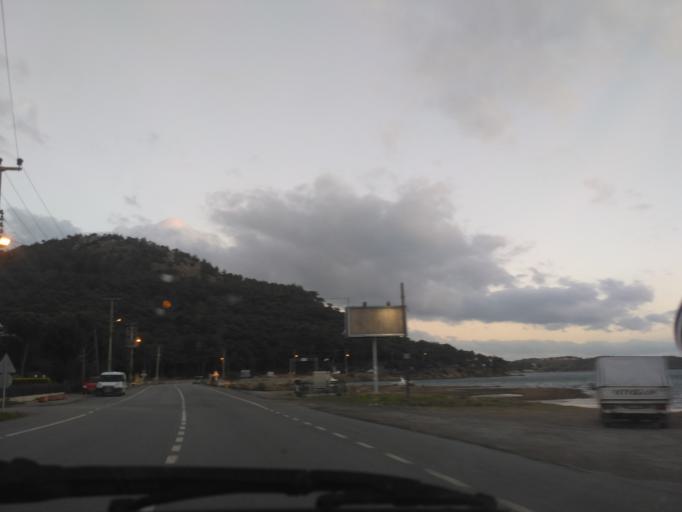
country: TR
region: Balikesir
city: Ayvalik
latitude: 39.2960
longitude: 26.6651
